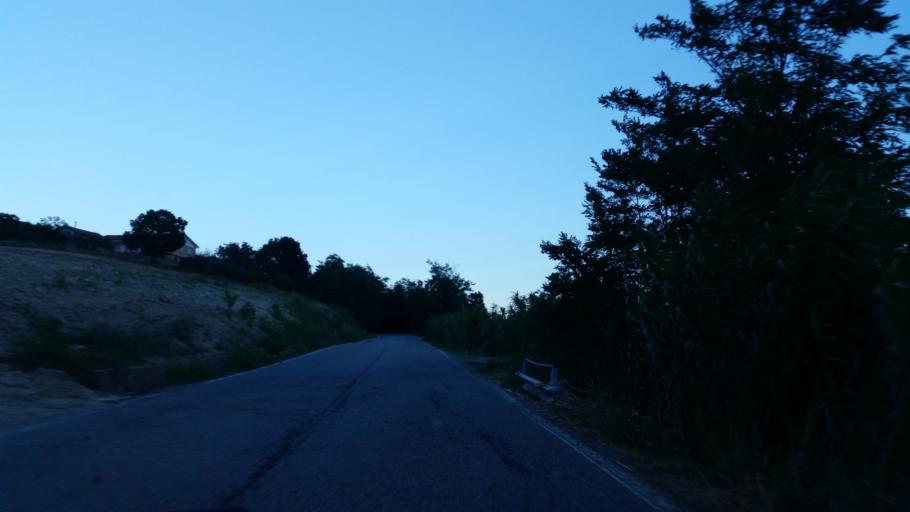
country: IT
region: Piedmont
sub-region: Provincia di Cuneo
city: Bricco di Neive
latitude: 44.7011
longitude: 8.1331
